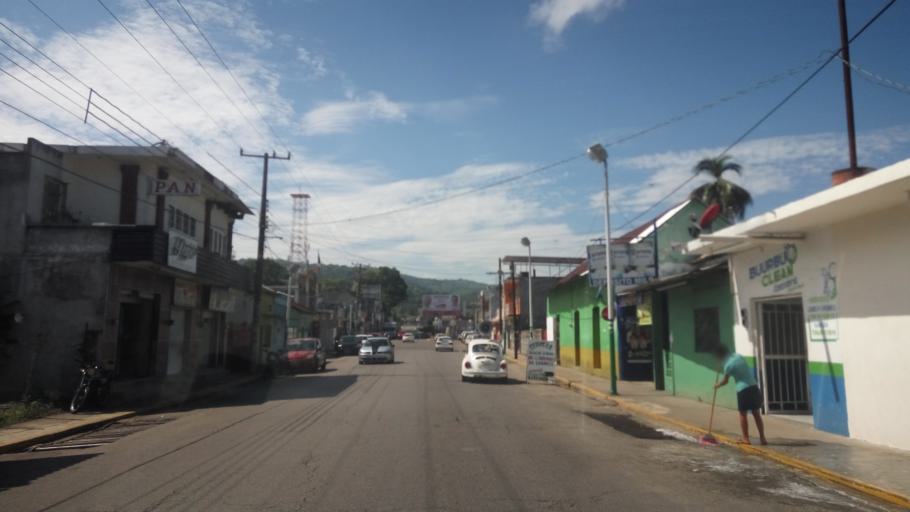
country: MX
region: Tabasco
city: Teapa
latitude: 17.5555
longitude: -92.9507
